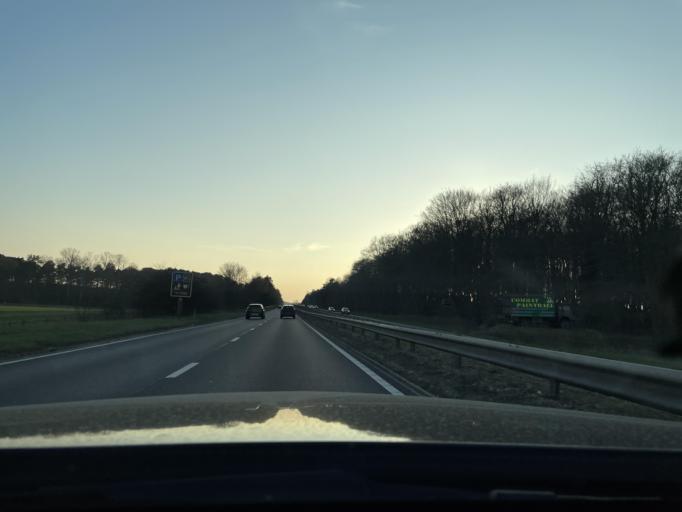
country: GB
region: England
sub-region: Norfolk
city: Shropham
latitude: 52.4513
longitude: 0.8595
